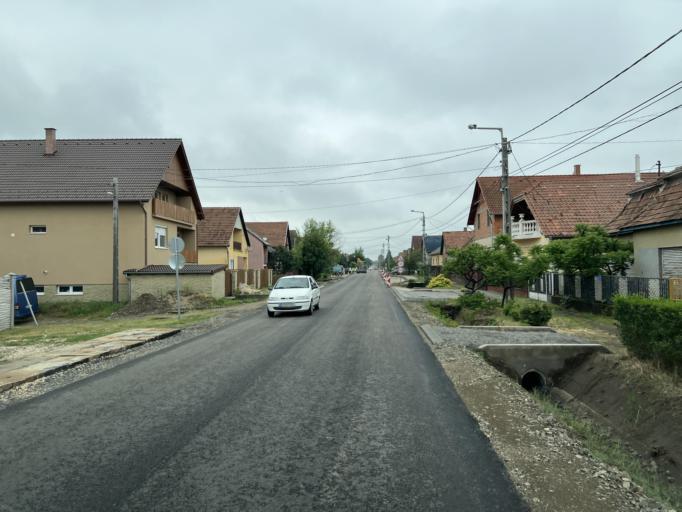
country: HU
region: Pest
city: Galgaheviz
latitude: 47.6154
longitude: 19.5795
